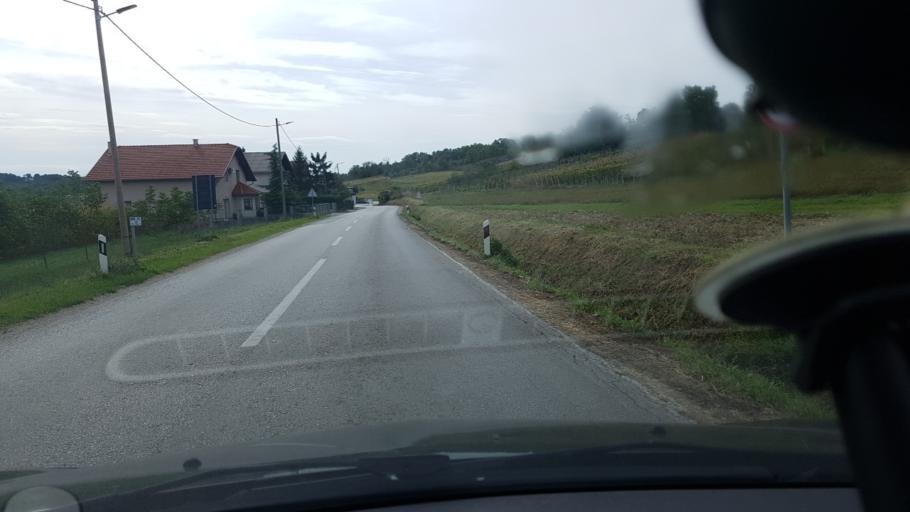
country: HR
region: Varazdinska
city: Ljubescica
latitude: 46.1086
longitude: 16.3790
